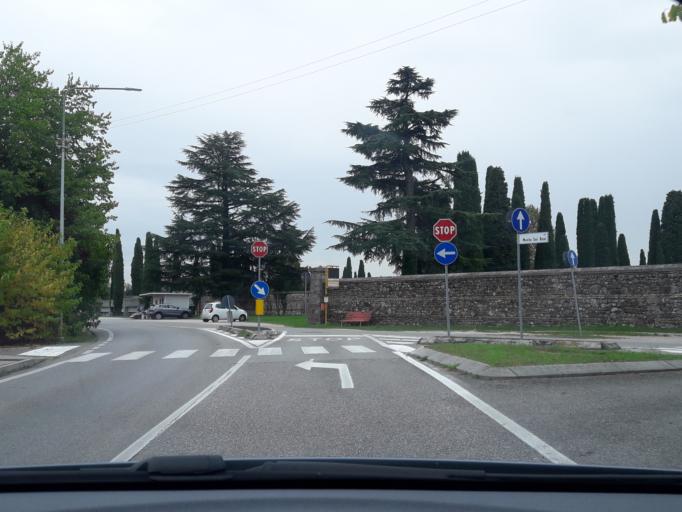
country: IT
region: Friuli Venezia Giulia
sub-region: Provincia di Udine
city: Udine
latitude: 46.0875
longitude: 13.2518
